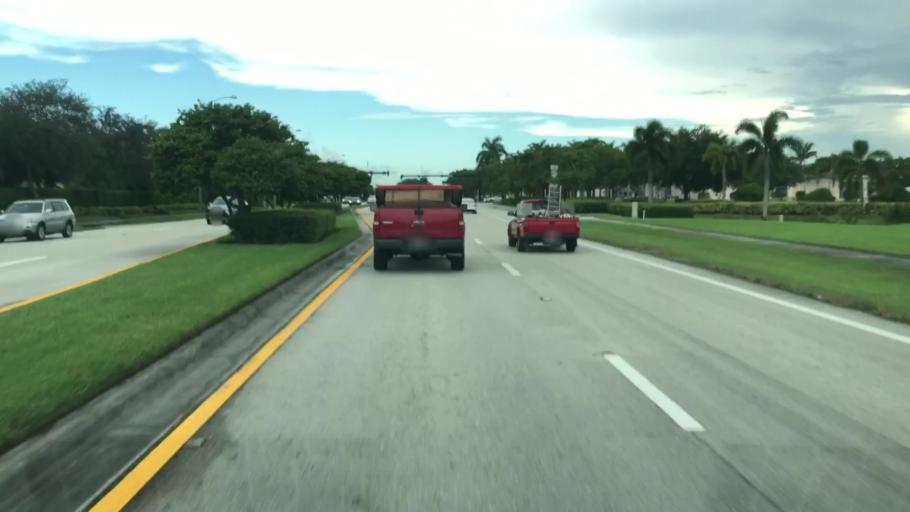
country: US
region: Florida
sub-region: Broward County
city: Coral Springs
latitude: 26.3079
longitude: -80.2789
